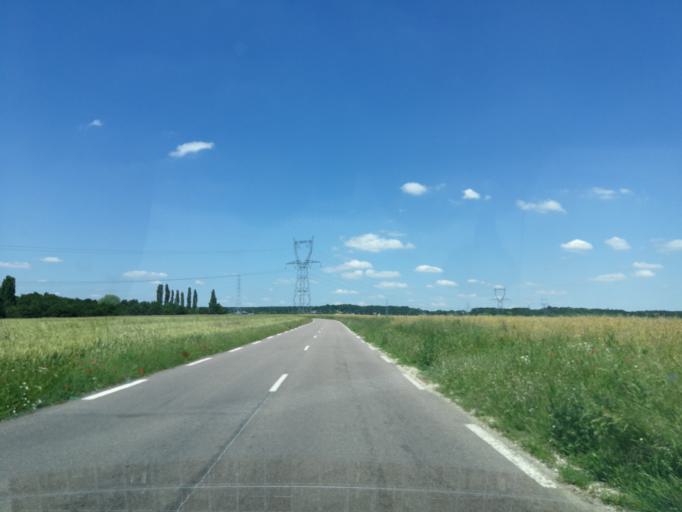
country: FR
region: Ile-de-France
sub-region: Departement de l'Essonne
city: Vaugrigneuse
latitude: 48.6091
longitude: 2.1259
